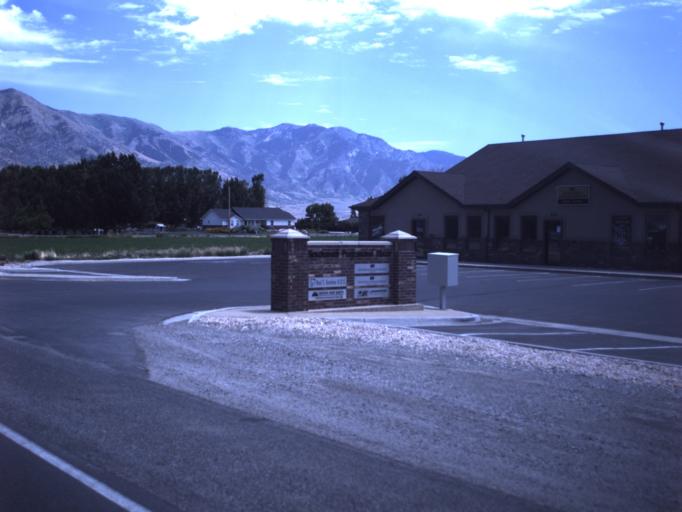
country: US
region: Utah
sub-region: Box Elder County
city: Tremonton
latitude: 41.7120
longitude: -112.1541
